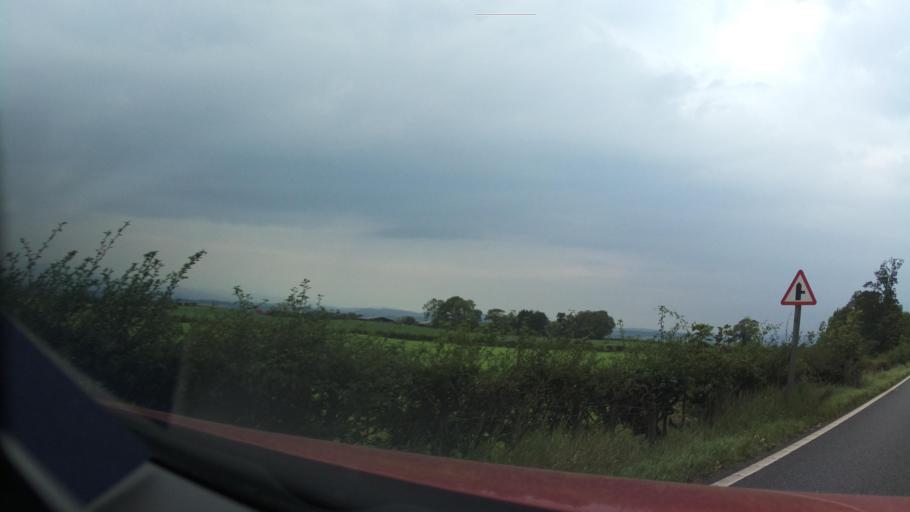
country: GB
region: Scotland
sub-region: Dumfries and Galloway
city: Lochmaben
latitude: 55.0602
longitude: -3.4821
